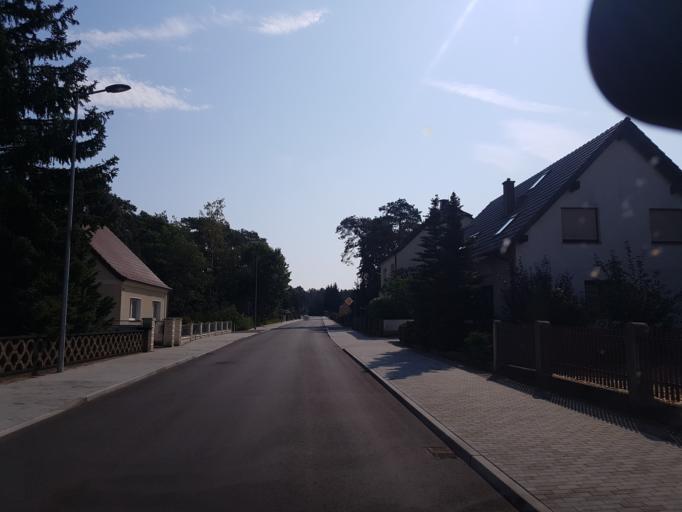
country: DE
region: Brandenburg
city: Lauchhammer
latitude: 51.5127
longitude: 13.7140
